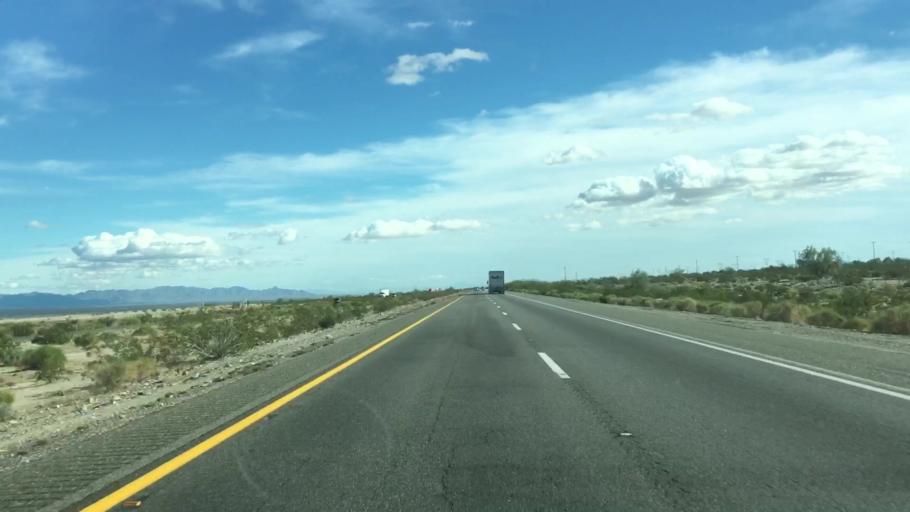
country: US
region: California
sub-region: Imperial County
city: Niland
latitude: 33.6909
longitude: -115.2723
